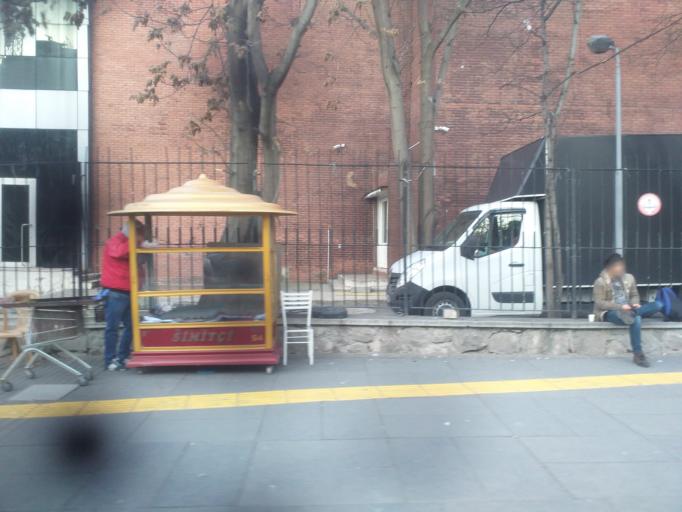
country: TR
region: Ankara
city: Ankara
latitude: 39.9360
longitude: 32.8248
